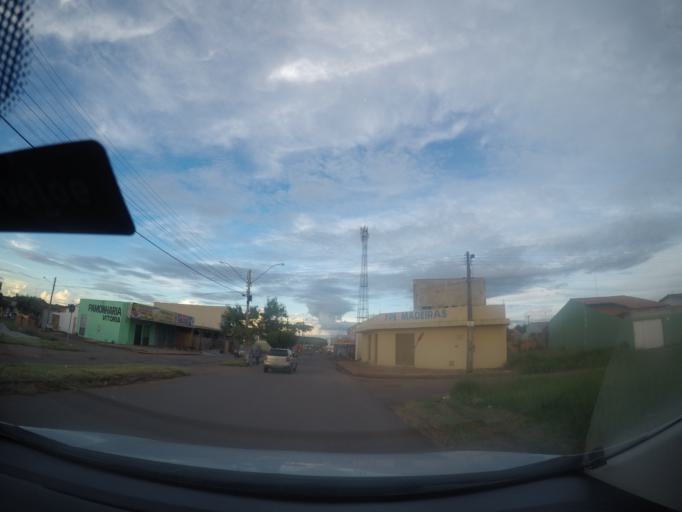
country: BR
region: Goias
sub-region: Goianira
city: Goianira
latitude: -16.5740
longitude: -49.3829
